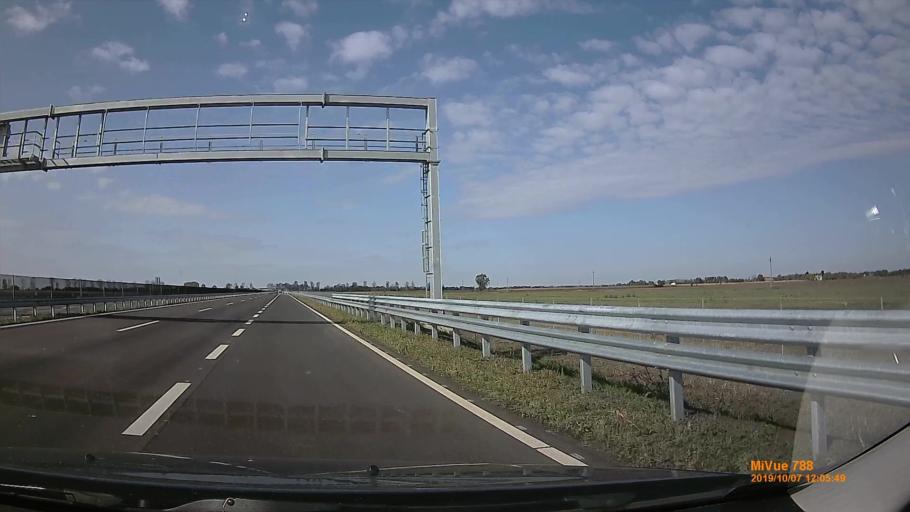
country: HU
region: Bekes
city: Bekesszentandras
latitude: 46.8209
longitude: 20.5115
